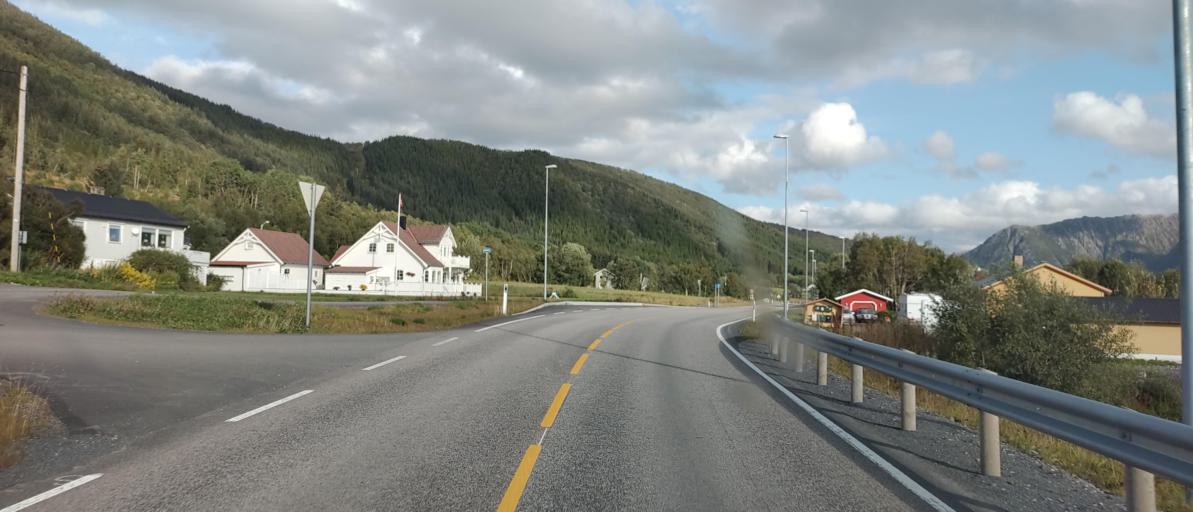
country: NO
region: Nordland
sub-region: Sortland
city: Sortland
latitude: 68.7517
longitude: 15.4773
